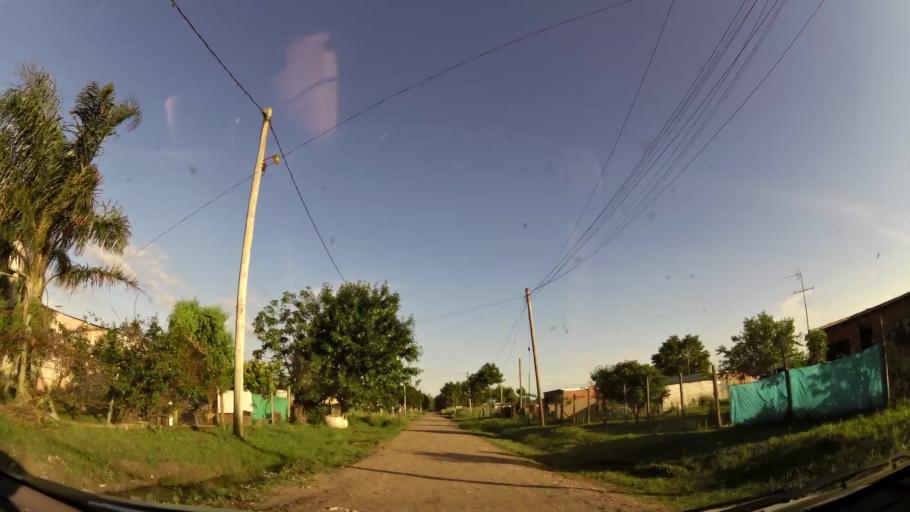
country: AR
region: Buenos Aires
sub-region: Partido de Merlo
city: Merlo
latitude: -34.7006
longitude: -58.7550
